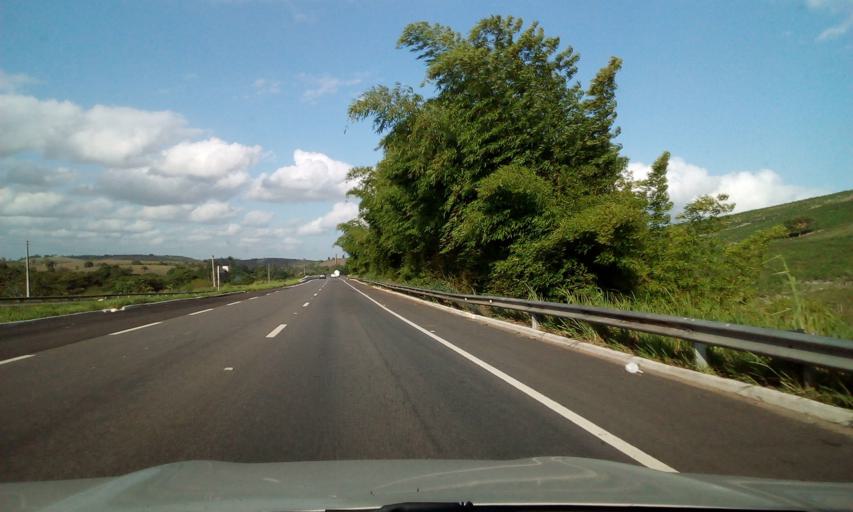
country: BR
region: Pernambuco
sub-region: Ribeirao
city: Ribeirao
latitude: -8.4528
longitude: -35.3563
